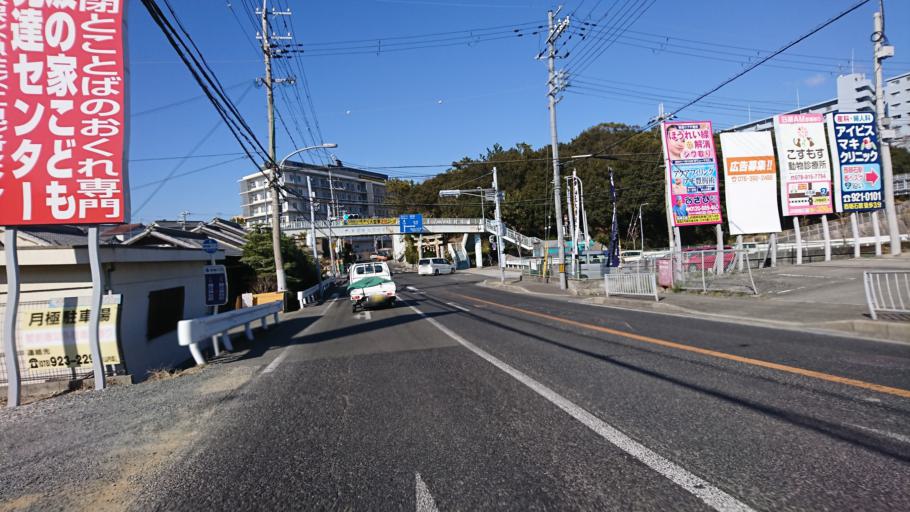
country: JP
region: Hyogo
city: Akashi
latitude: 34.6594
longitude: 134.9515
